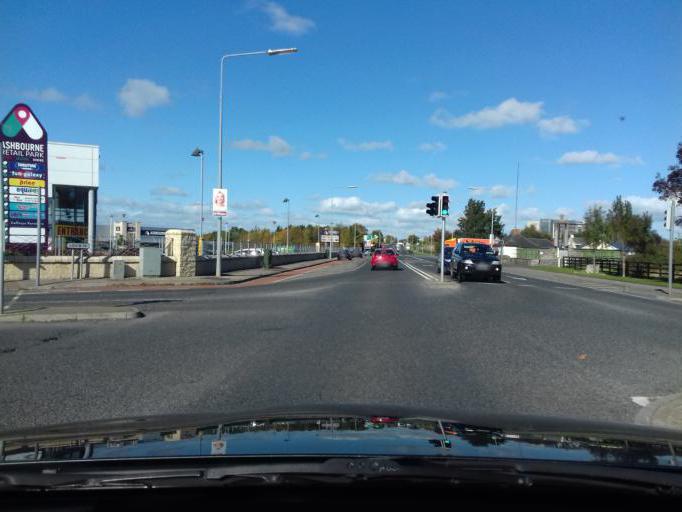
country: IE
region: Leinster
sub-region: An Mhi
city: Ashbourne
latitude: 53.5218
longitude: -6.4119
